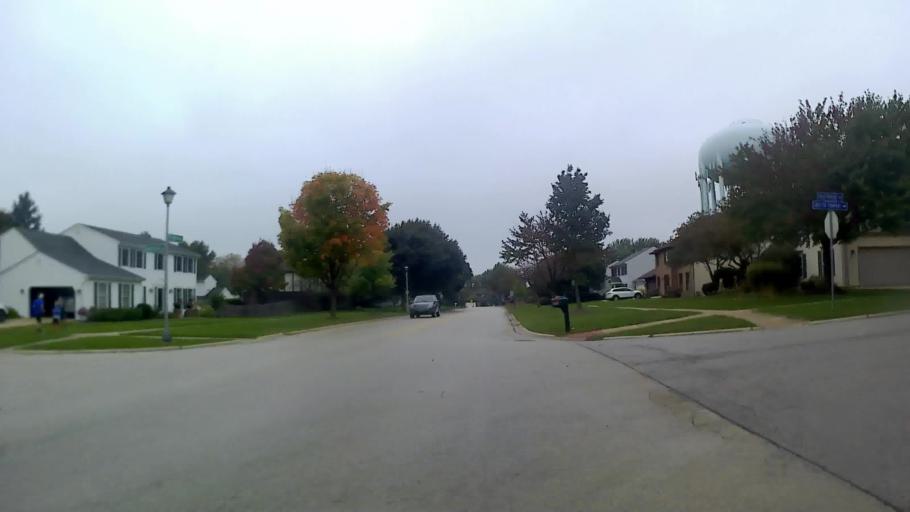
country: US
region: Illinois
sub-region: DuPage County
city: Wheaton
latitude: 41.8361
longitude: -88.1191
